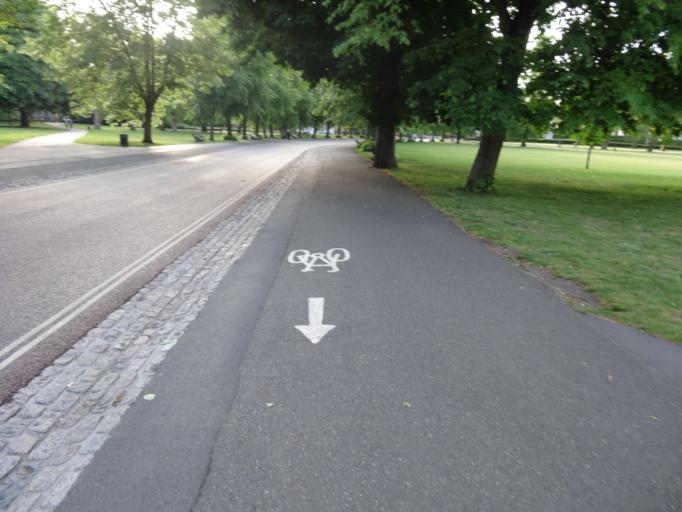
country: GB
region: England
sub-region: Greater London
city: Blackheath
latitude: 51.4785
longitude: -0.0049
